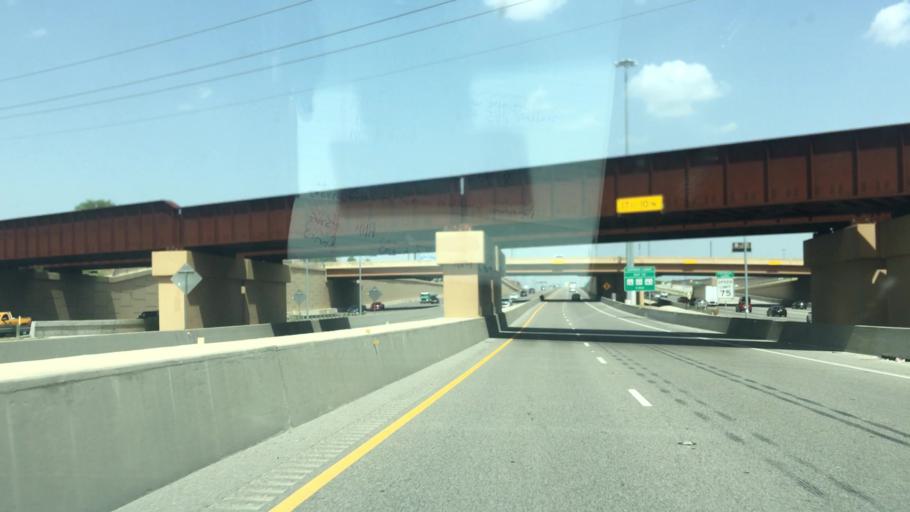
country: US
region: Texas
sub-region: Tarrant County
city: Watauga
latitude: 32.8402
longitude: -97.2533
